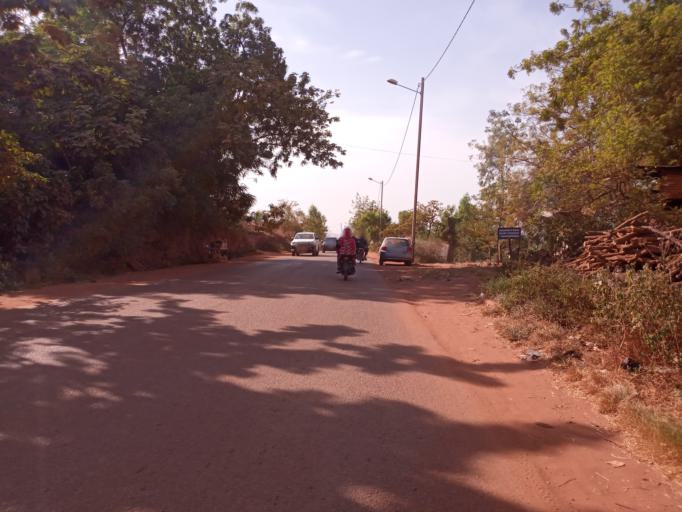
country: ML
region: Bamako
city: Bamako
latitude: 12.6292
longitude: -7.9502
